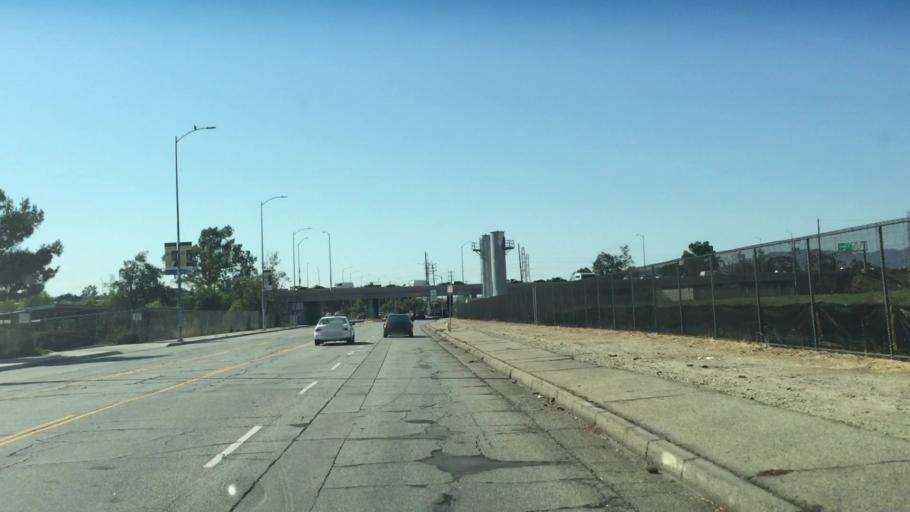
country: US
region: California
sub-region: Los Angeles County
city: Van Nuys
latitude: 34.2258
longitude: -118.4093
